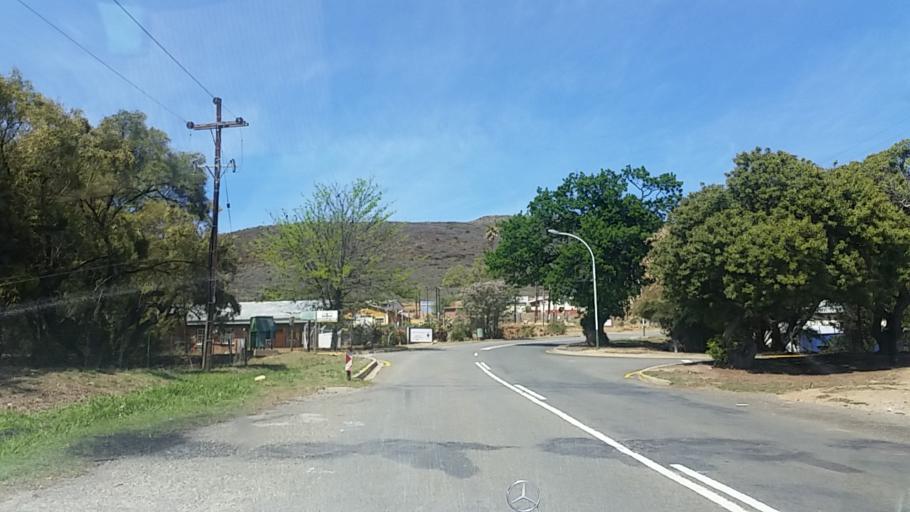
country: ZA
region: Western Cape
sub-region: Eden District Municipality
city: Knysna
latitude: -33.6544
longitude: 23.1348
